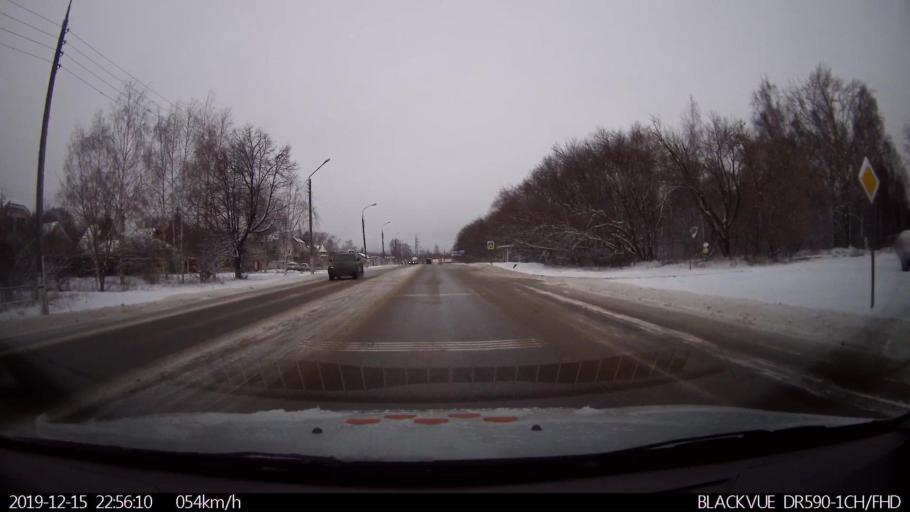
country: RU
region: Nizjnij Novgorod
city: Afonino
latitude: 56.2239
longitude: 44.0980
